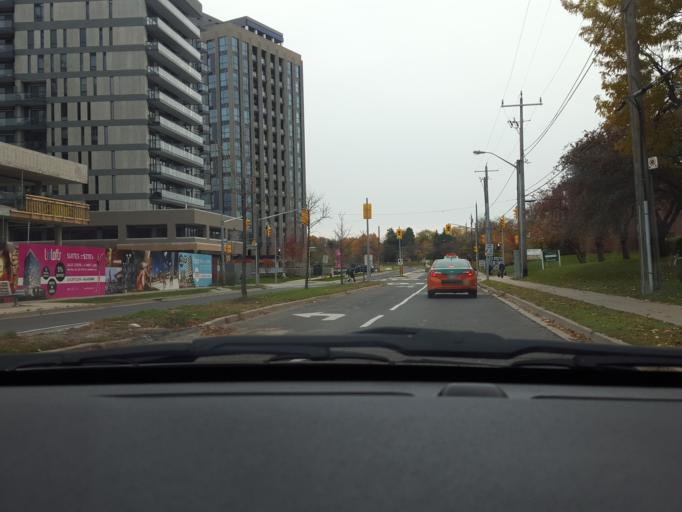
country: CA
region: Ontario
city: Willowdale
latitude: 43.7335
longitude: -79.3472
